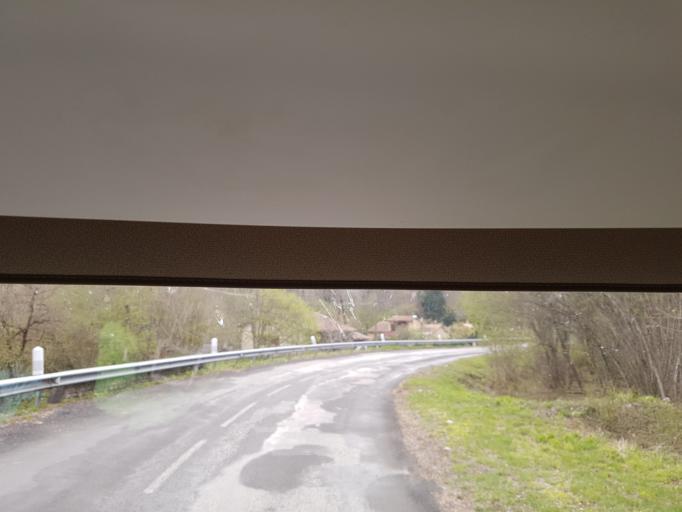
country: FR
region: Languedoc-Roussillon
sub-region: Departement de l'Aude
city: Quillan
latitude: 42.7750
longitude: 2.1625
